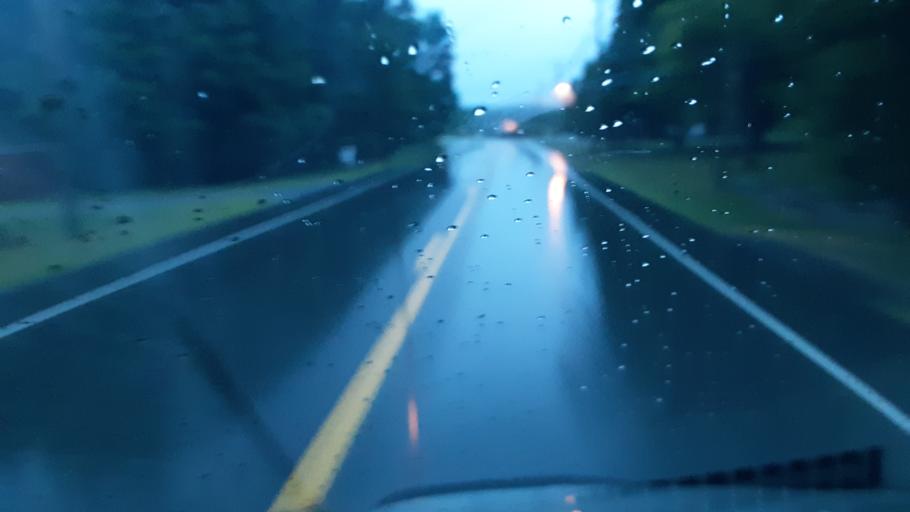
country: US
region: Maine
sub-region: Penobscot County
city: Patten
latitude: 45.8782
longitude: -68.4183
